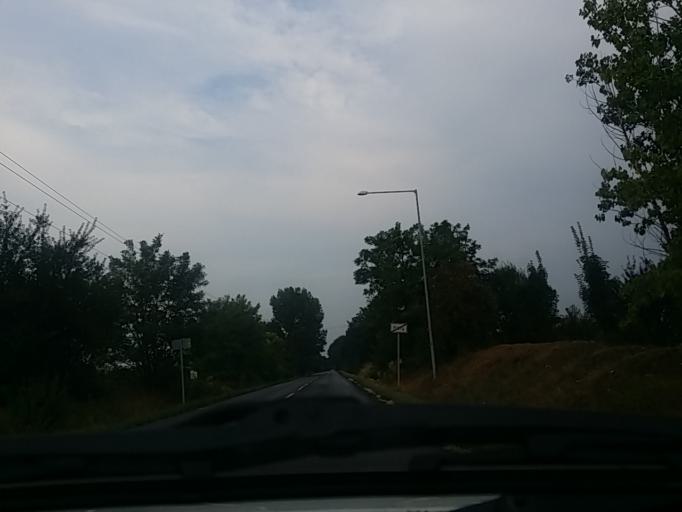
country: HU
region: Pest
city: Paty
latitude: 47.5135
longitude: 18.8095
